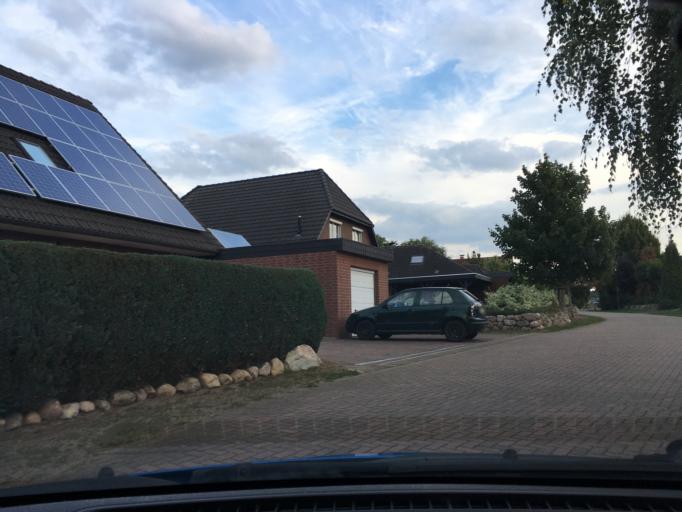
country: DE
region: Lower Saxony
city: Westergellersen
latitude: 53.2371
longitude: 10.2521
